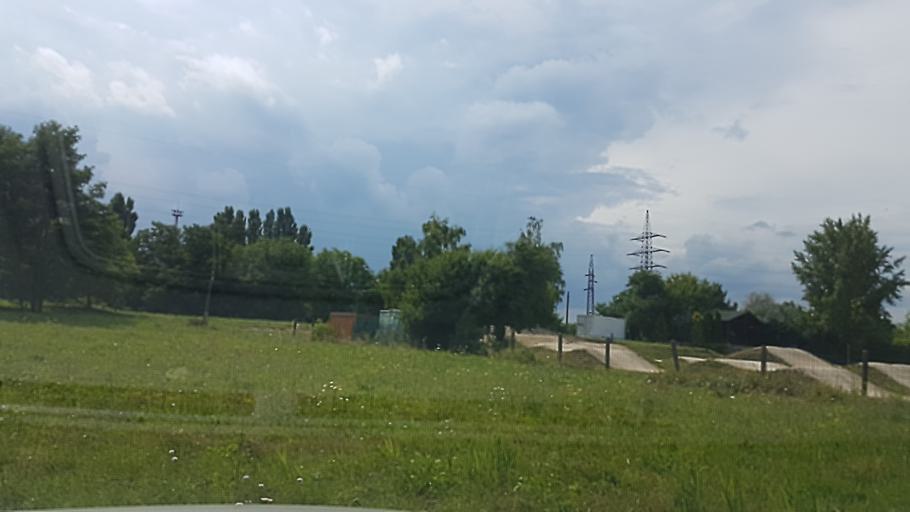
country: HU
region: Gyor-Moson-Sopron
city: Sopron
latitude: 47.6960
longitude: 16.5702
